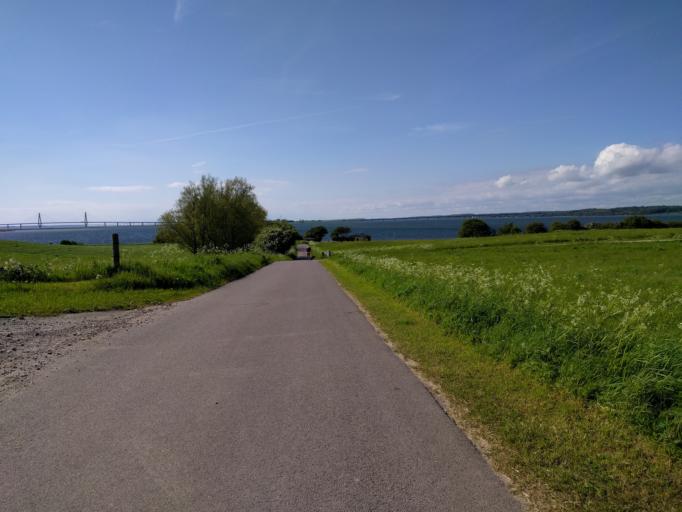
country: DK
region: Zealand
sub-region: Guldborgsund Kommune
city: Stubbekobing
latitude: 54.9357
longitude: 12.0317
